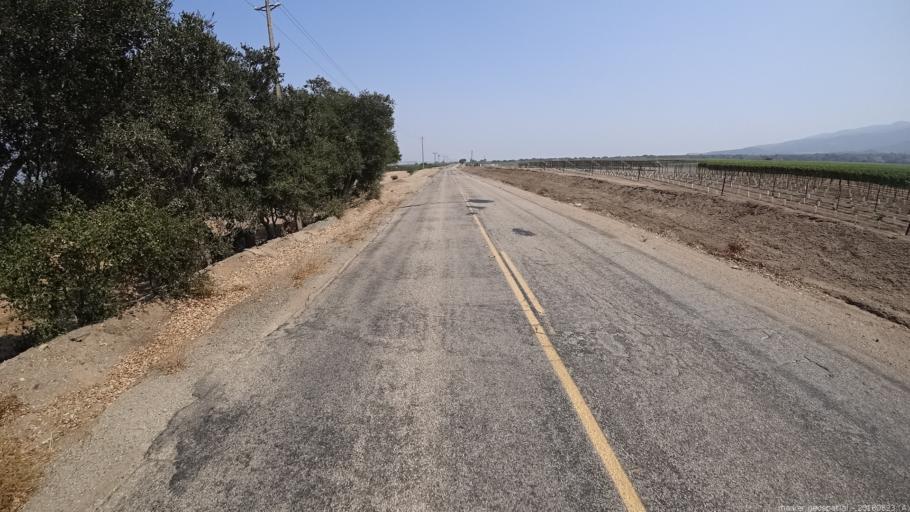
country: US
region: California
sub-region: Monterey County
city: Gonzales
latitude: 36.4373
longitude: -121.4284
